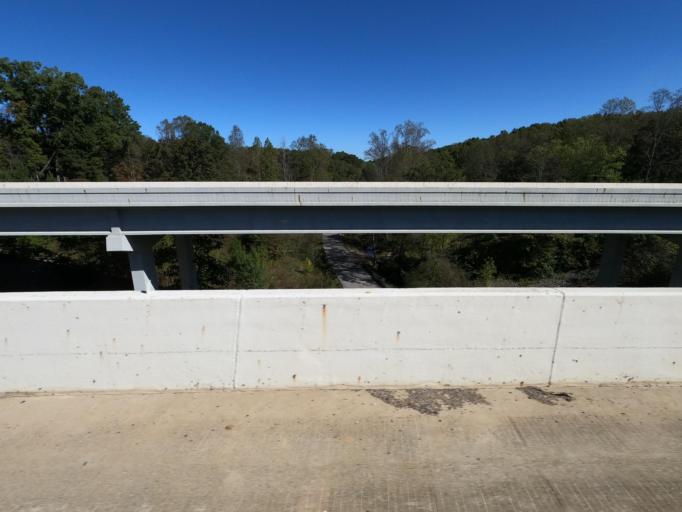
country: US
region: Tennessee
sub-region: Williamson County
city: Fairview
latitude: 35.8595
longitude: -87.0818
